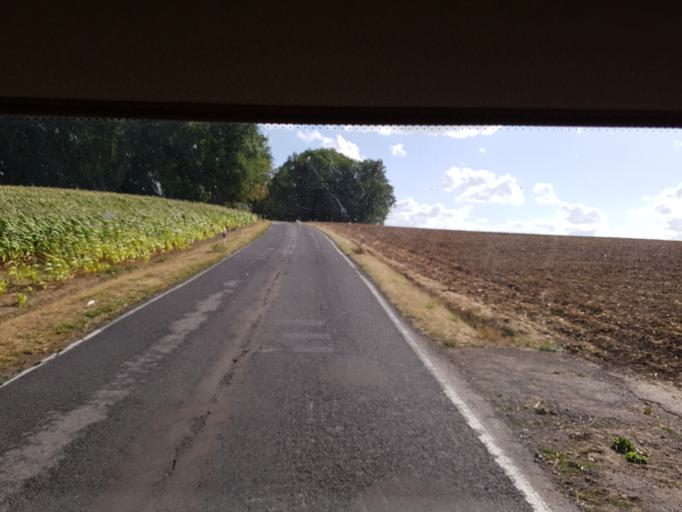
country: DE
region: Rheinland-Pfalz
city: Kirf
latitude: 49.5635
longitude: 6.4559
